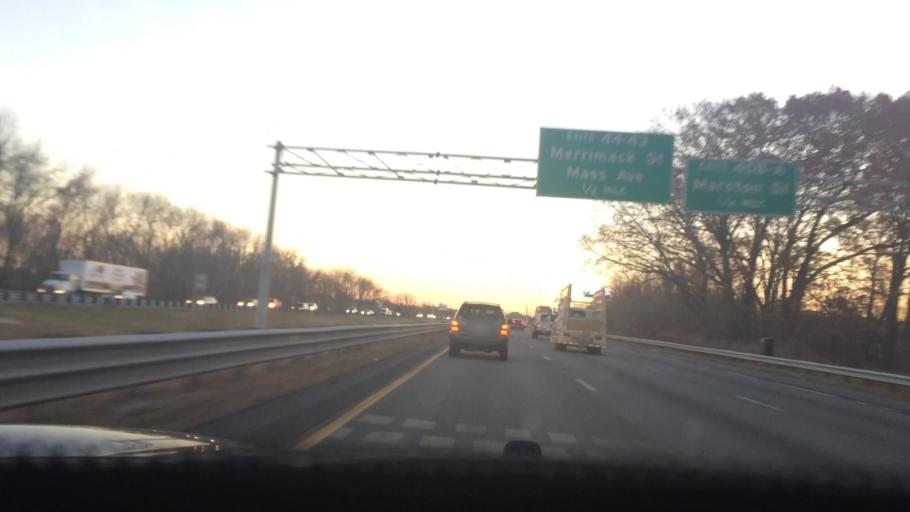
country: US
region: Massachusetts
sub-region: Essex County
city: North Andover
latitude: 42.7209
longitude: -71.1373
